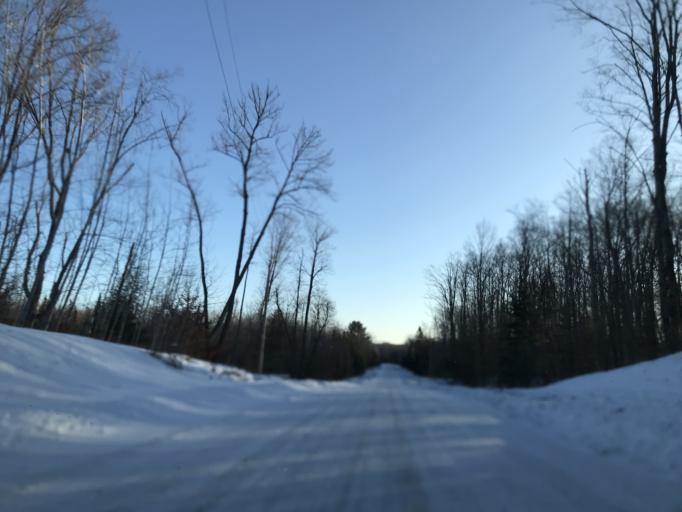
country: US
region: Michigan
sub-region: Menominee County
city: Menominee
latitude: 45.2906
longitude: -87.7027
